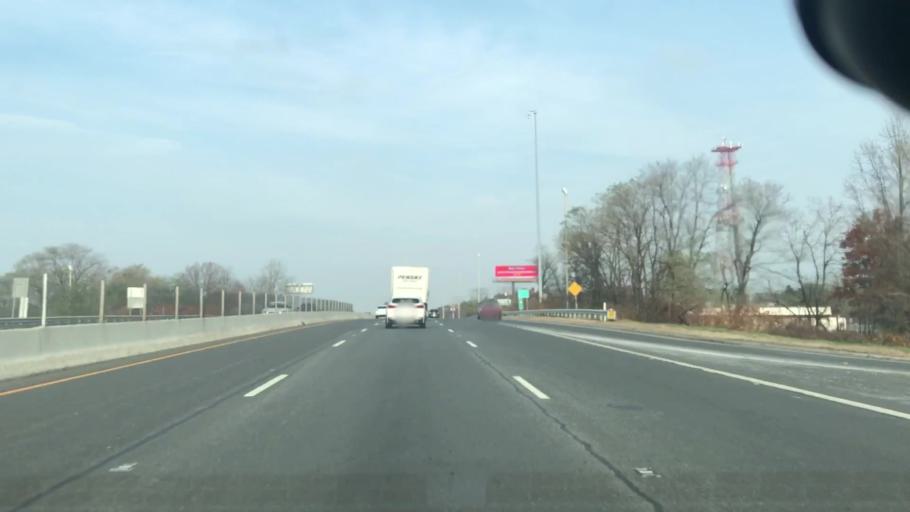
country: US
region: New Jersey
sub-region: Middlesex County
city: Madison Park
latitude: 40.4531
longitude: -74.2973
